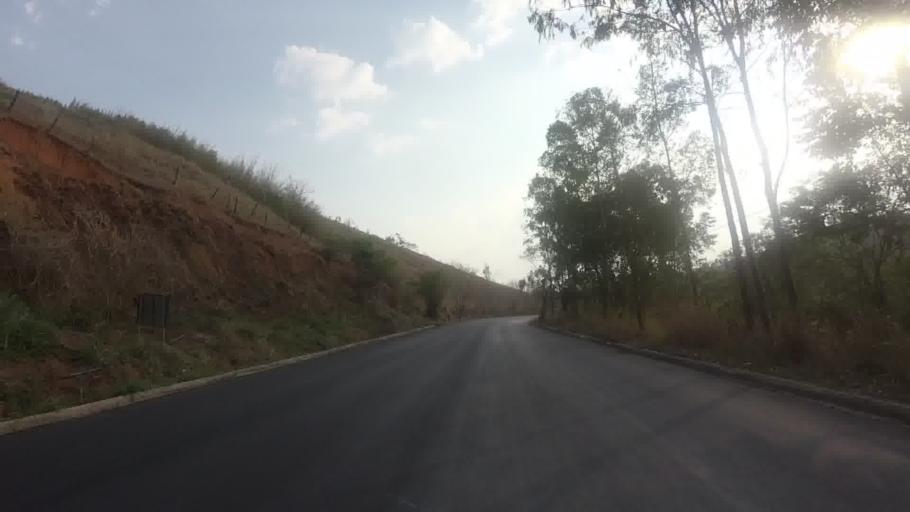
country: BR
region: Rio de Janeiro
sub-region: Itaperuna
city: Itaperuna
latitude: -21.3689
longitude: -41.9408
